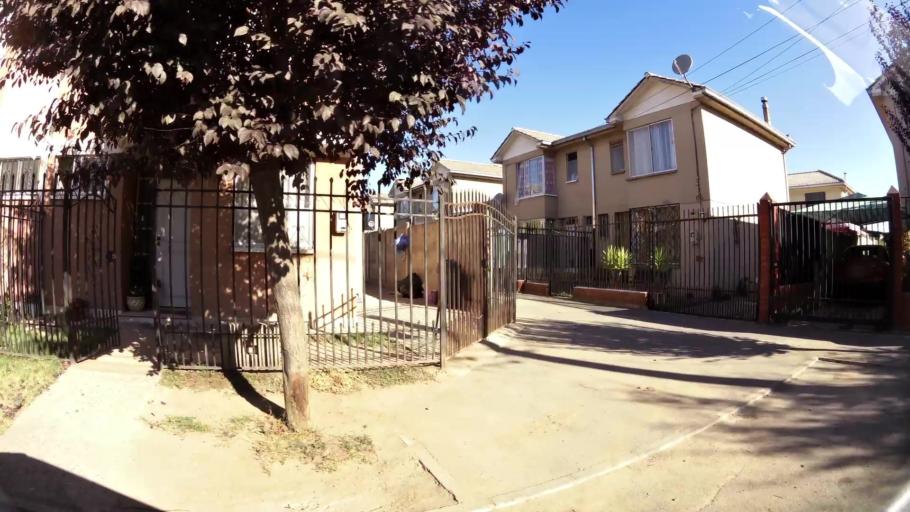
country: CL
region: O'Higgins
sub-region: Provincia de Cachapoal
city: Rancagua
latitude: -34.1799
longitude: -70.7589
